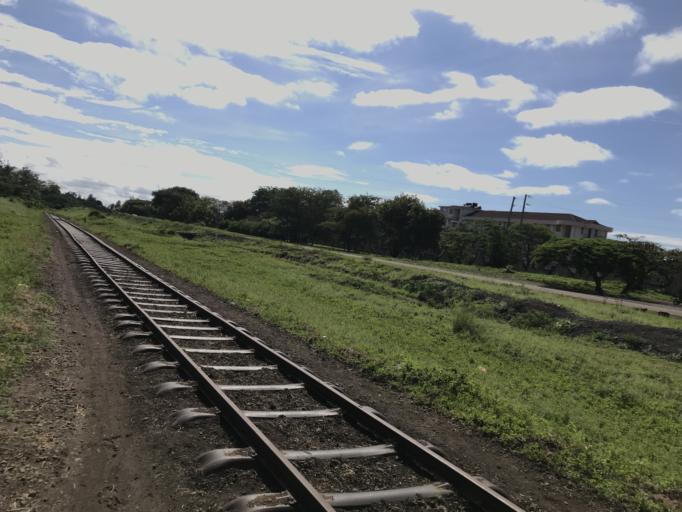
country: TZ
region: Arusha
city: Usa River
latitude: -3.3978
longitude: 36.7979
